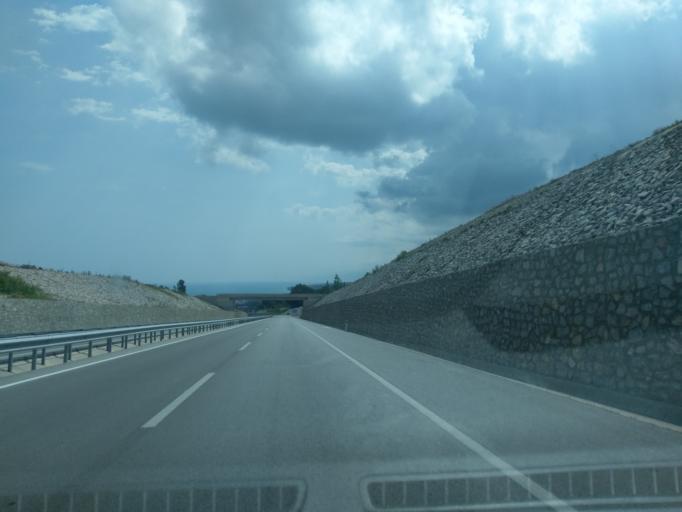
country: TR
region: Sinop
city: Kabali
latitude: 41.8515
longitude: 35.1204
